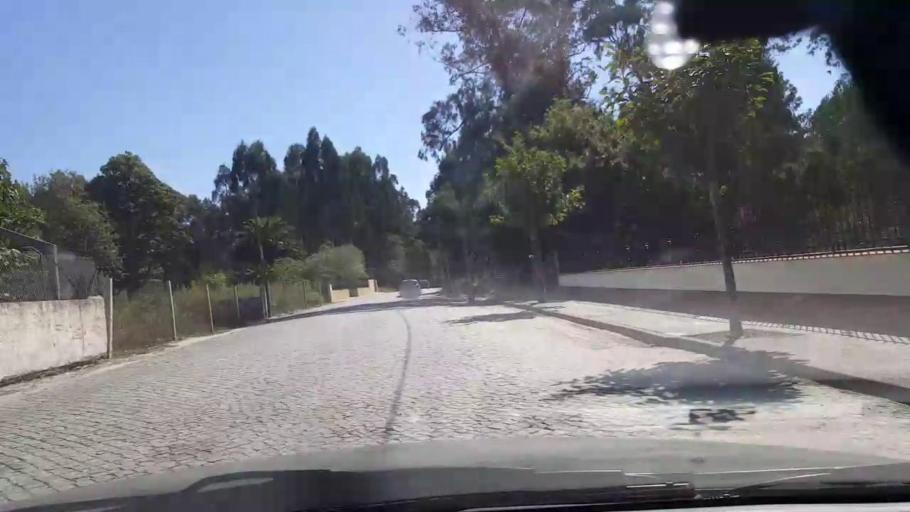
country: PT
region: Porto
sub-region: Vila do Conde
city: Arvore
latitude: 41.3290
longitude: -8.7285
